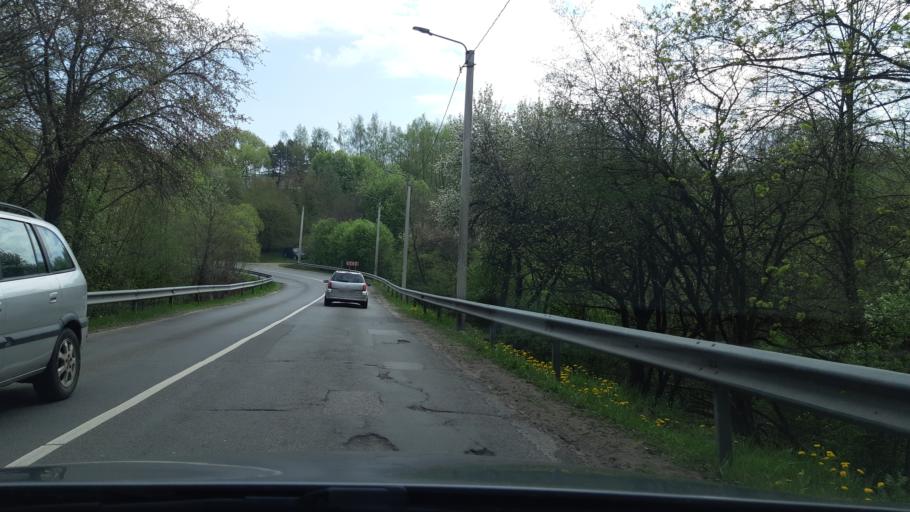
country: LT
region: Kauno apskritis
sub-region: Kaunas
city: Silainiai
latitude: 54.9227
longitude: 23.8615
